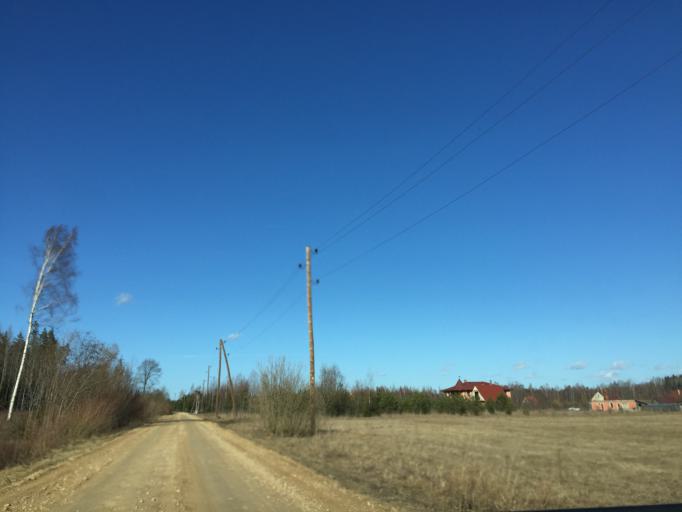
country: LV
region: Ogre
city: Ogre
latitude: 56.8749
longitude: 24.7084
